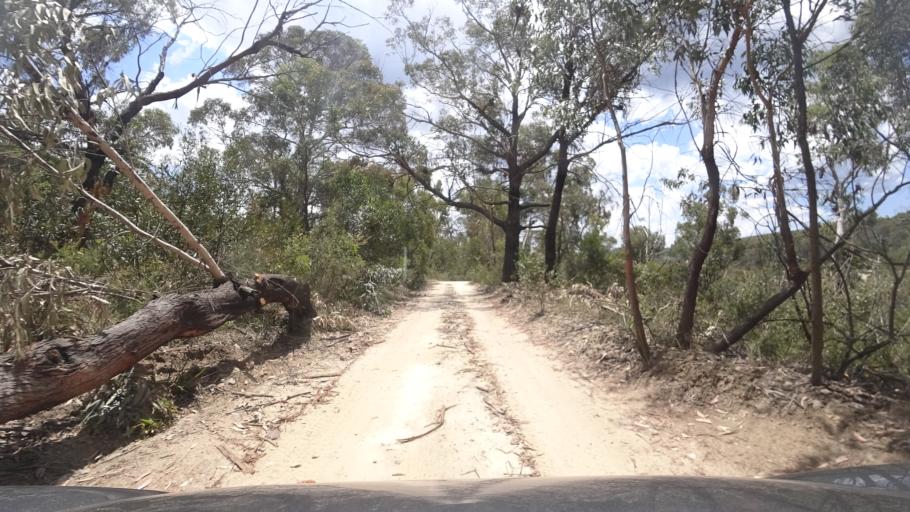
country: AU
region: New South Wales
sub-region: Lithgow
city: Lithgow
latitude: -33.4794
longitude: 150.2464
